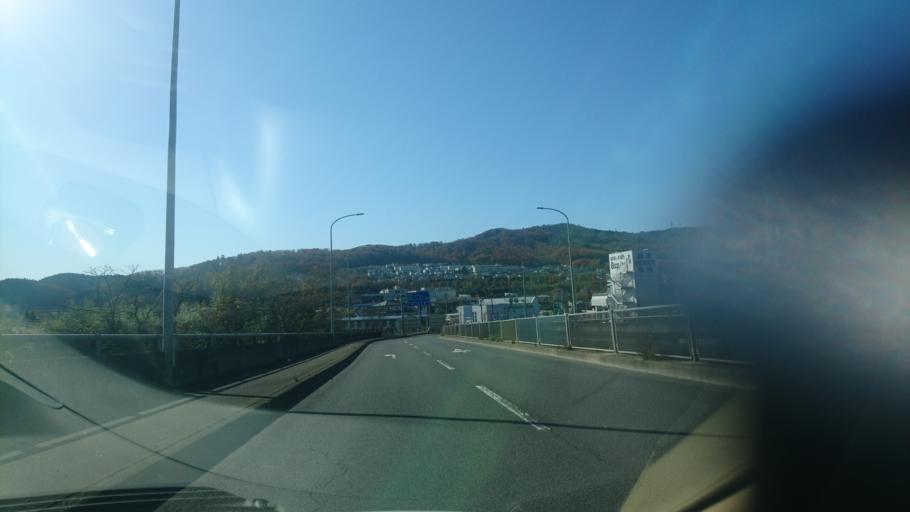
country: JP
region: Miyagi
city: Sendai
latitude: 38.2675
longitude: 140.8127
